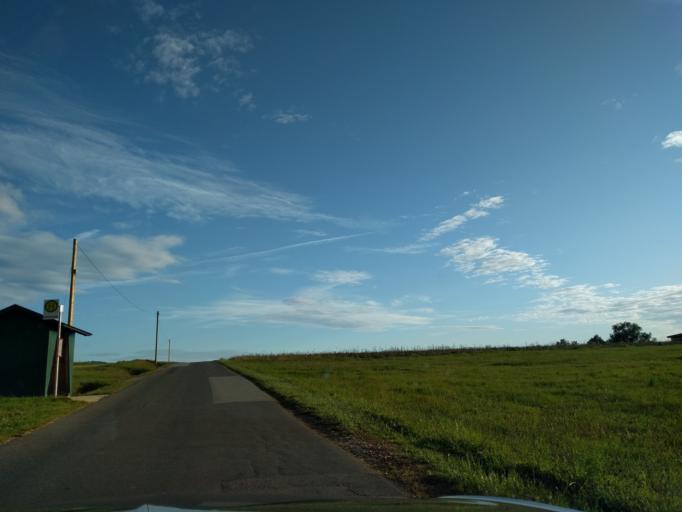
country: DE
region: Bavaria
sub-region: Upper Palatinate
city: Grafenwiesen
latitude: 49.1804
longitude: 12.8844
